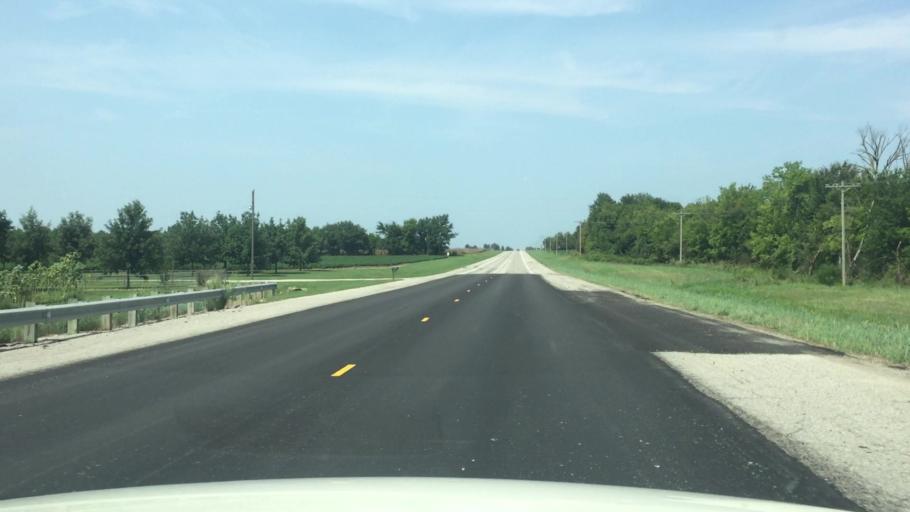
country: US
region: Kansas
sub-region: Crawford County
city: Pittsburg
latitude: 37.2558
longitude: -94.7051
